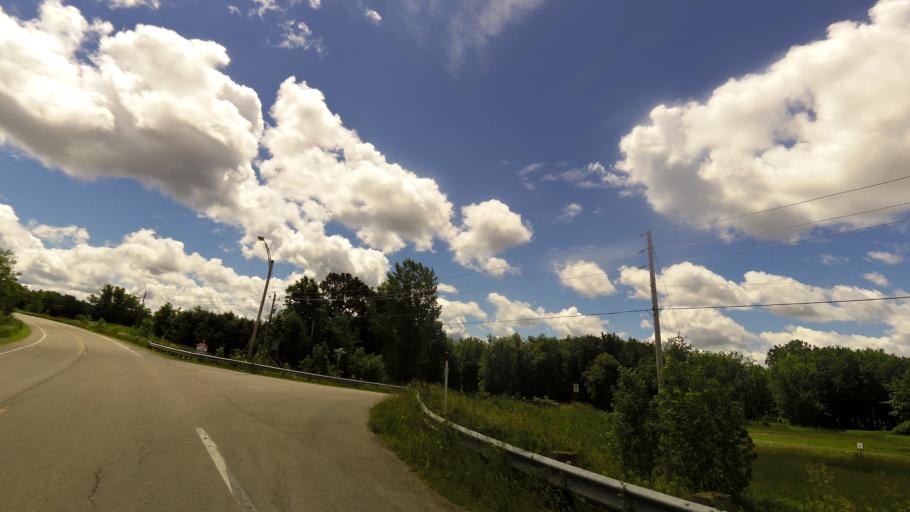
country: CA
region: Quebec
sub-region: Monteregie
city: Rigaud
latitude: 45.5330
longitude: -74.3027
